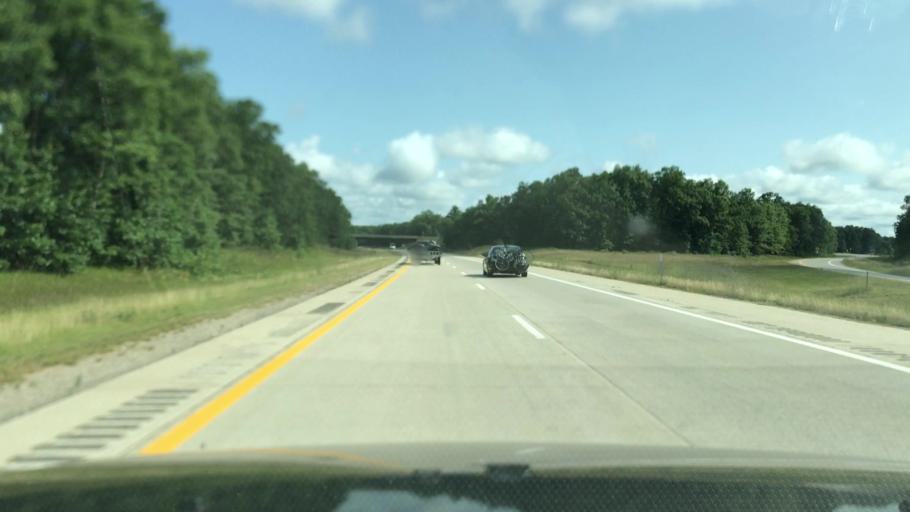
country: US
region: Michigan
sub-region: Montcalm County
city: Howard City
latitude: 43.4205
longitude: -85.4979
